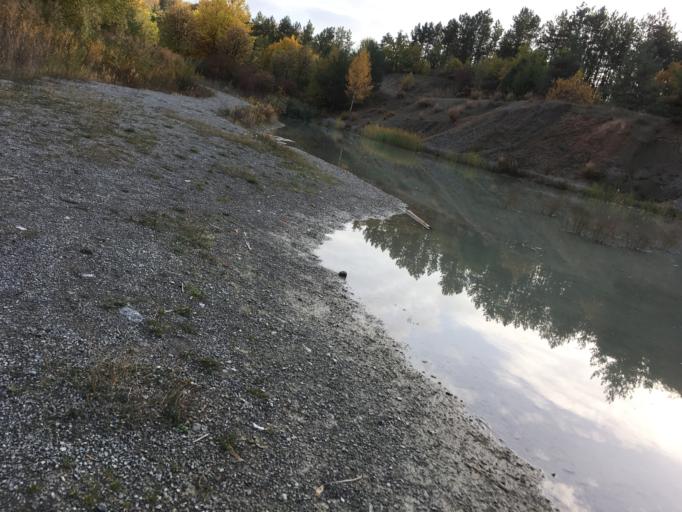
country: DE
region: Baden-Wuerttemberg
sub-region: Karlsruhe Region
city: Seckach
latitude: 49.4818
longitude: 9.3466
